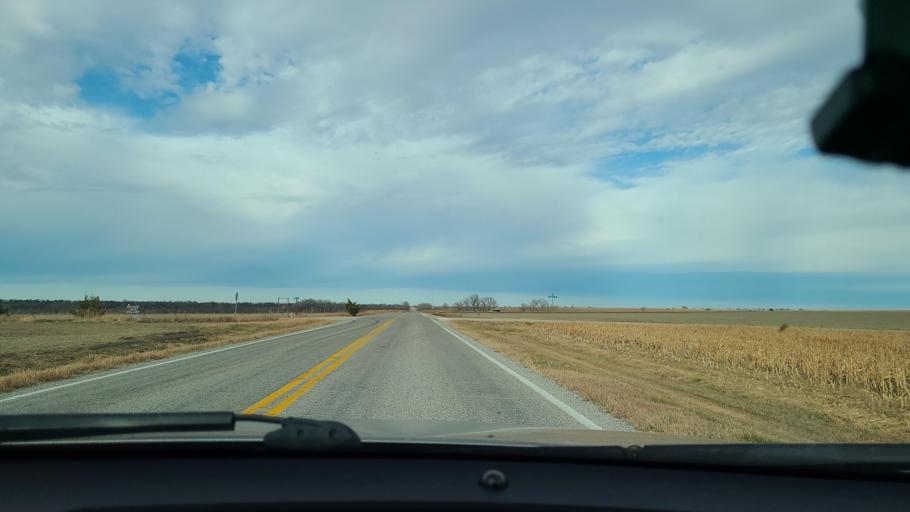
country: US
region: Kansas
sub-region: McPherson County
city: Inman
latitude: 38.3326
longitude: -97.9246
